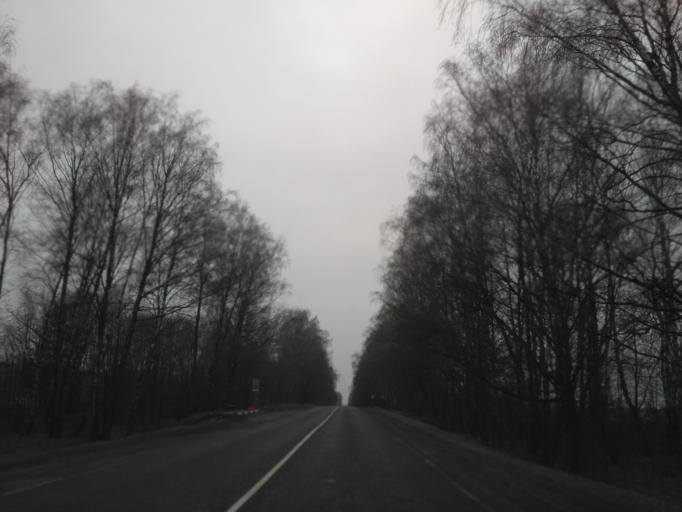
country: BY
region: Minsk
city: Snow
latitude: 53.2380
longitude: 26.2348
